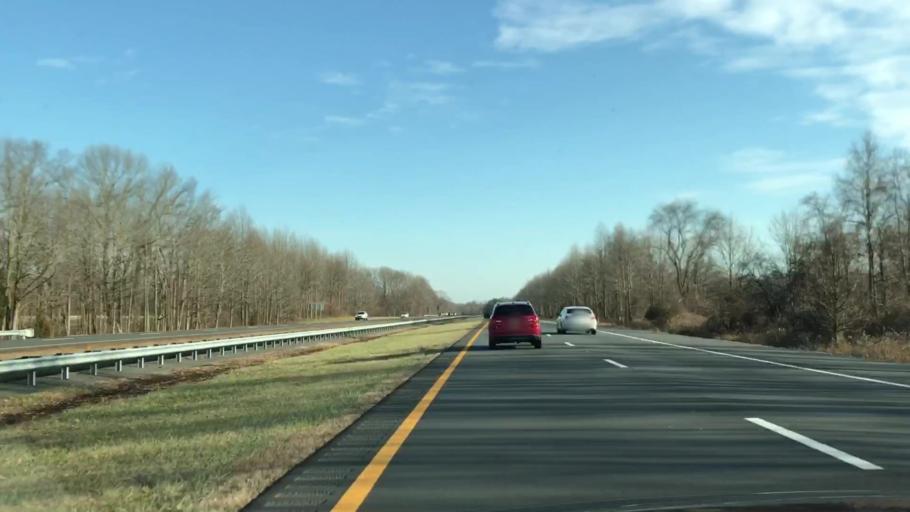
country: US
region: New Jersey
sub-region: Monmouth County
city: Shrewsbury
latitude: 40.1806
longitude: -74.5551
